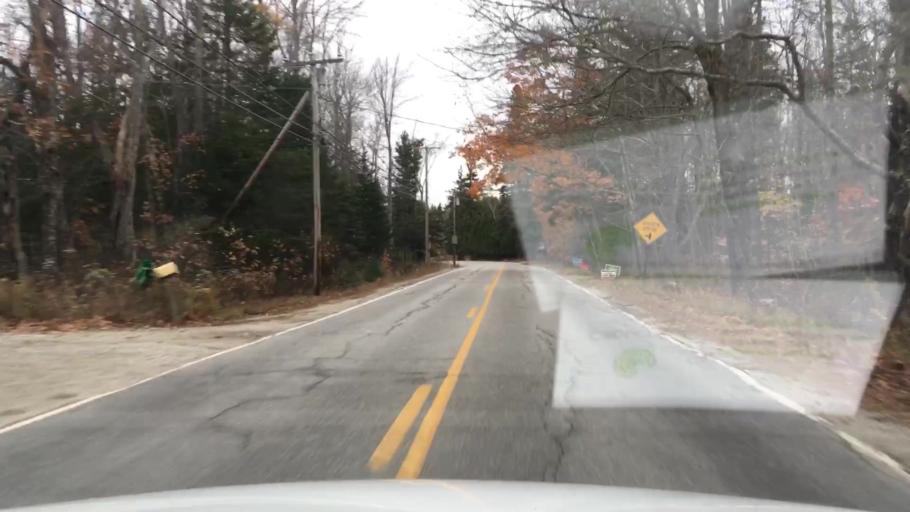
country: US
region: Maine
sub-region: Hancock County
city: Sedgwick
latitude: 44.3671
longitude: -68.5537
